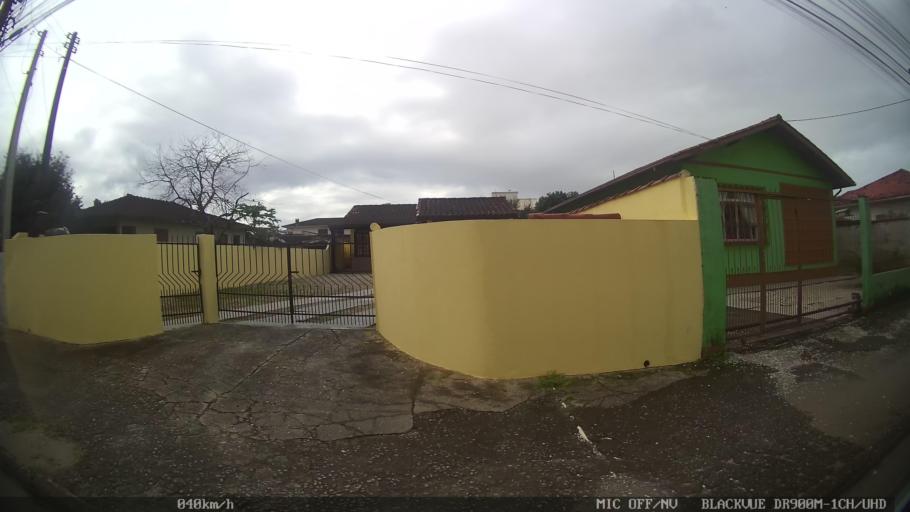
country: BR
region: Santa Catarina
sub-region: Biguacu
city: Biguacu
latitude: -27.5074
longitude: -48.6500
